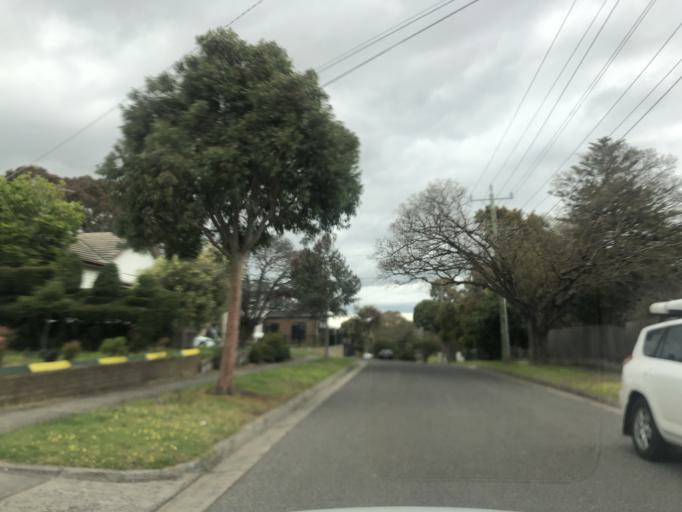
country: AU
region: Victoria
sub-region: Greater Dandenong
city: Dandenong
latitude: -37.9747
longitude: 145.1957
